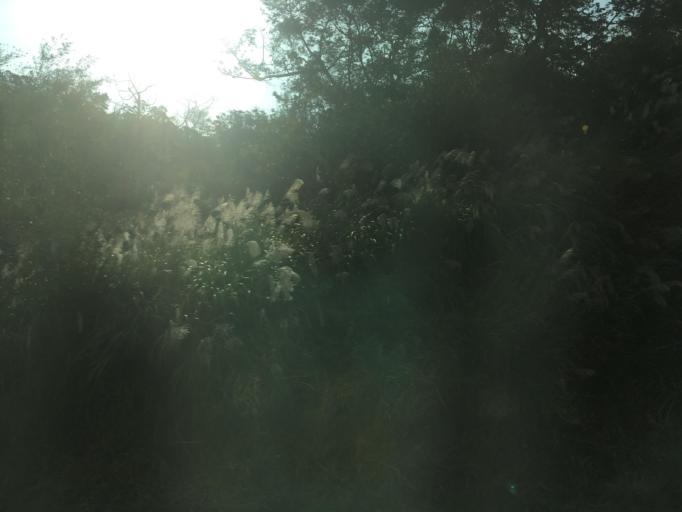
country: TW
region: Taiwan
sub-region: Miaoli
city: Miaoli
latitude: 24.6225
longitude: 120.8629
